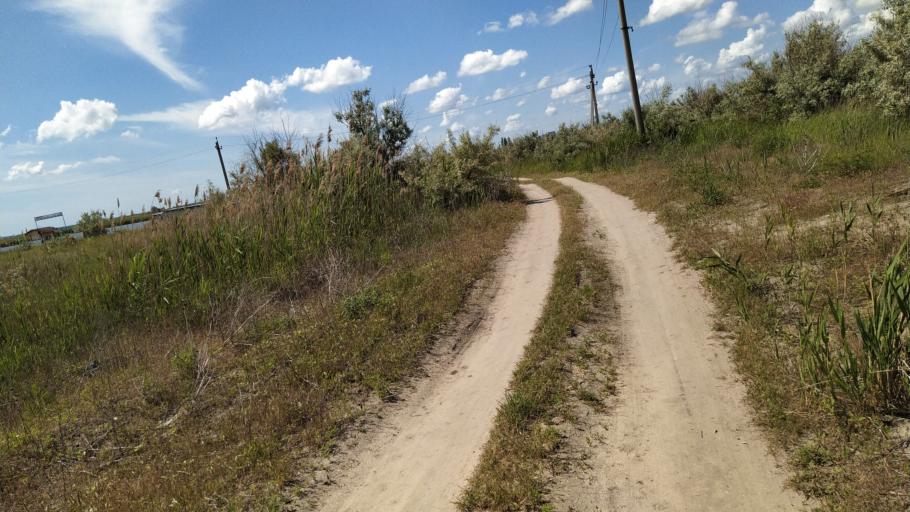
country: RU
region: Rostov
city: Bataysk
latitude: 47.1421
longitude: 39.6679
